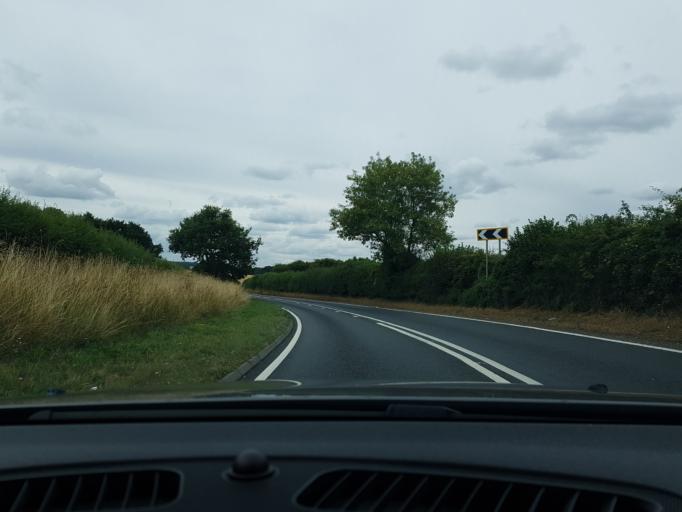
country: GB
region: England
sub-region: Hampshire
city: Tadley
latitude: 51.2954
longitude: -1.1714
